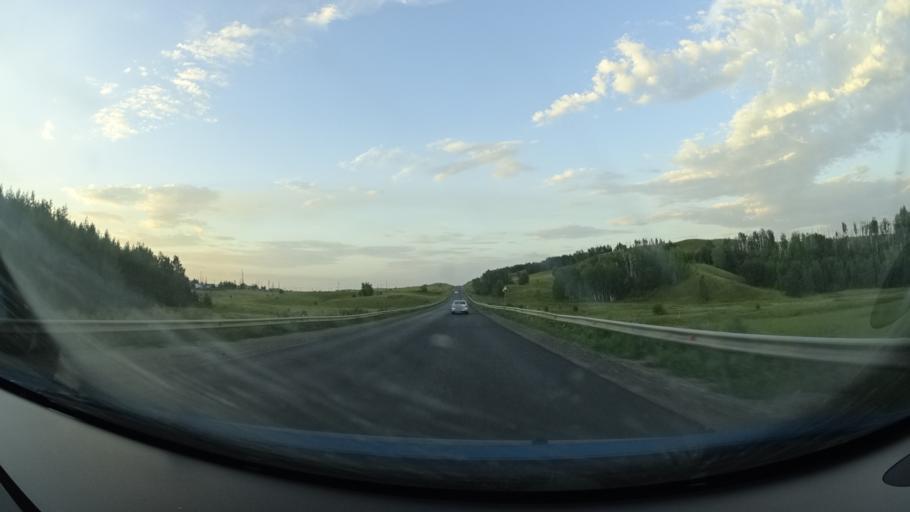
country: RU
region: Orenburg
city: Severnoye
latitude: 54.1663
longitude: 52.6388
